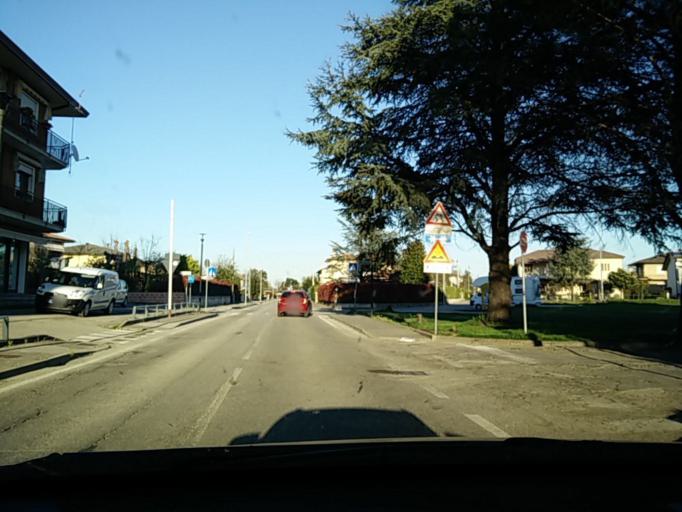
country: IT
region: Veneto
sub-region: Provincia di Treviso
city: Roncade
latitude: 45.6138
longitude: 12.3796
